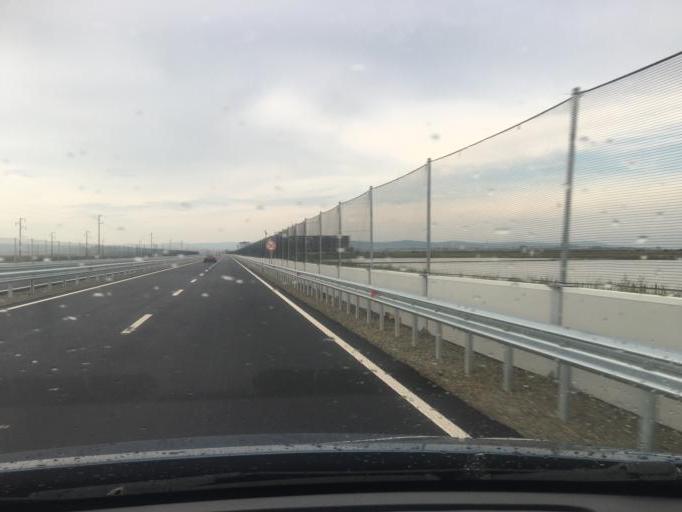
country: BG
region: Burgas
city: Aheloy
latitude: 42.6214
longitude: 27.6277
